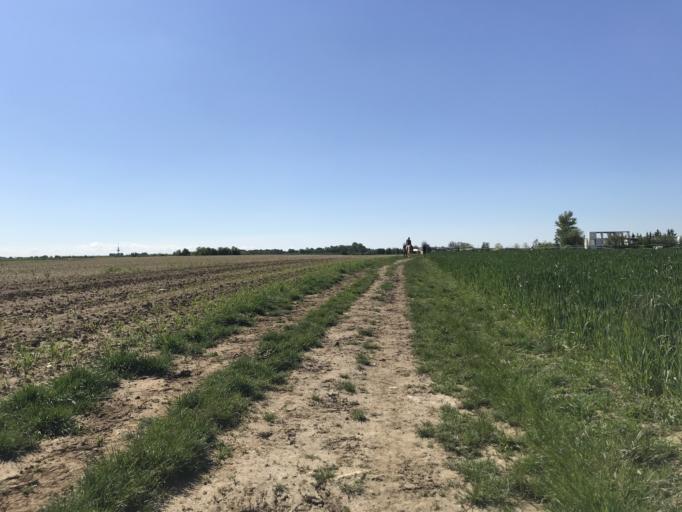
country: DE
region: Rheinland-Pfalz
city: Wackernheim
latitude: 49.9702
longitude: 8.1218
